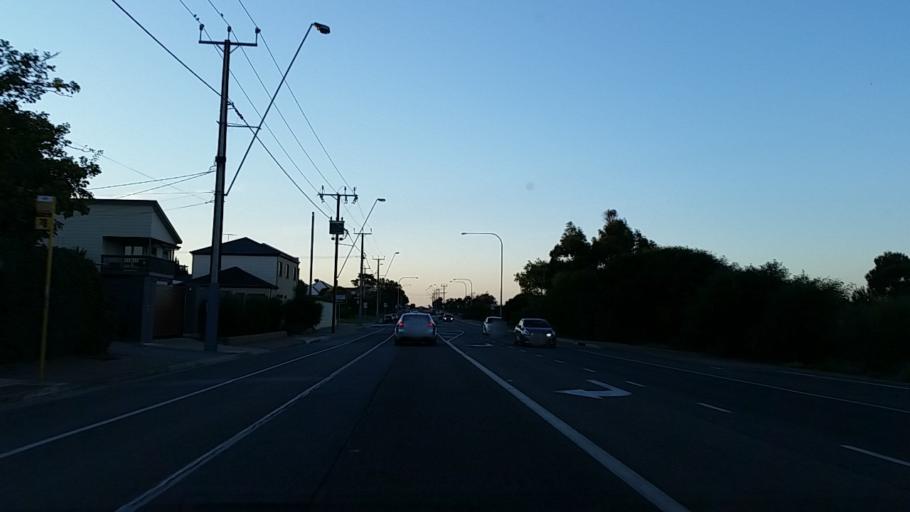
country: AU
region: South Australia
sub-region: Adelaide
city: Port Noarlunga
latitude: -35.1612
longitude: 138.4752
